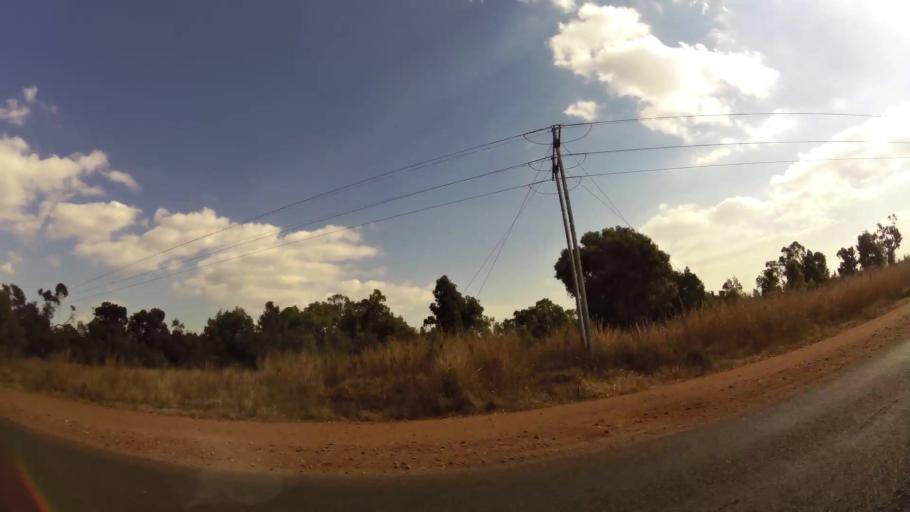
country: ZA
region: Gauteng
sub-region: Ekurhuleni Metropolitan Municipality
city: Tembisa
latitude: -26.0100
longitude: 28.2517
